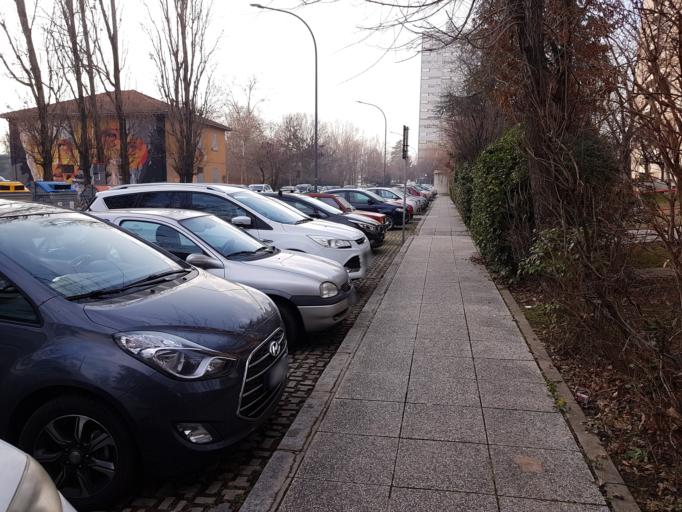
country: IT
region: Emilia-Romagna
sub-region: Provincia di Bologna
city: Quarto Inferiore
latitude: 44.5114
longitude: 11.3943
